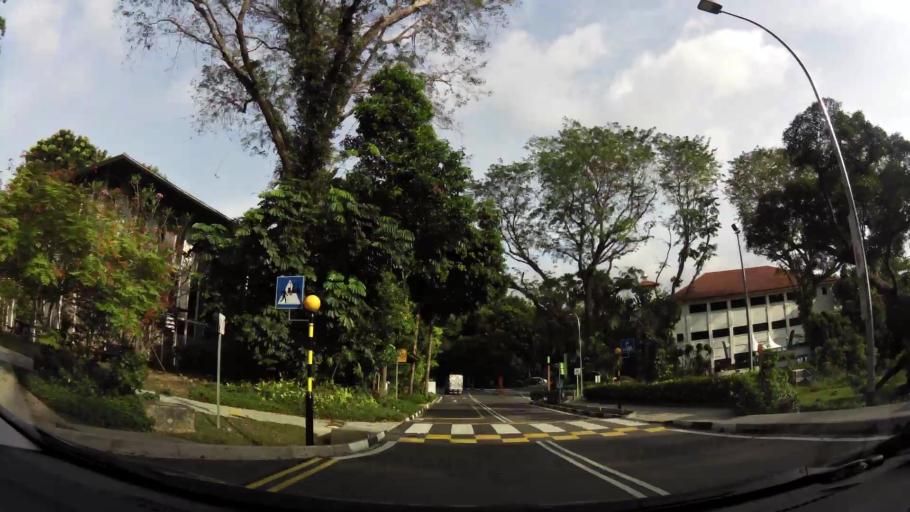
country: SG
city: Singapore
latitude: 1.2478
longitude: 103.8277
